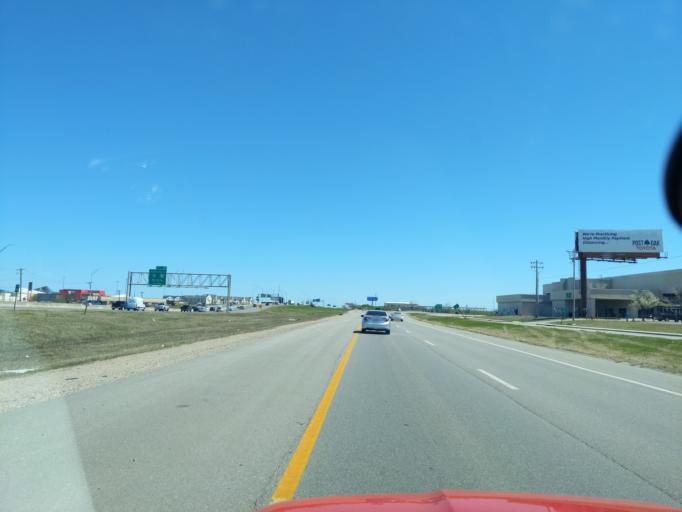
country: US
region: Oklahoma
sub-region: Cleveland County
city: Moore
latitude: 35.3917
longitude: -97.5009
